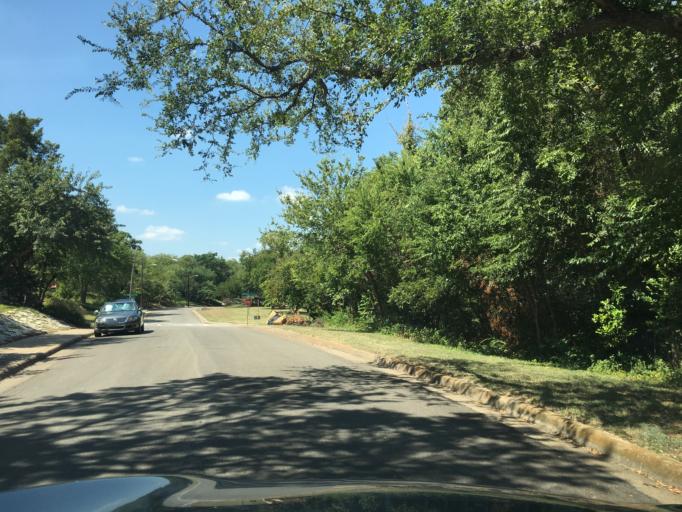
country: US
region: Texas
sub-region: Dallas County
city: Garland
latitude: 32.8521
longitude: -96.6904
